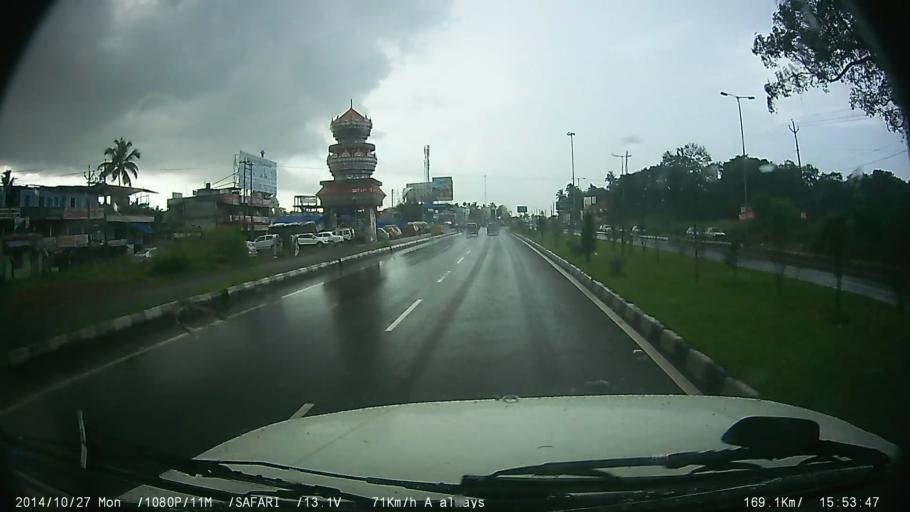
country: IN
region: Kerala
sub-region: Thrissur District
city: Kizhake Chalakudi
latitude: 10.2665
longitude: 76.3509
